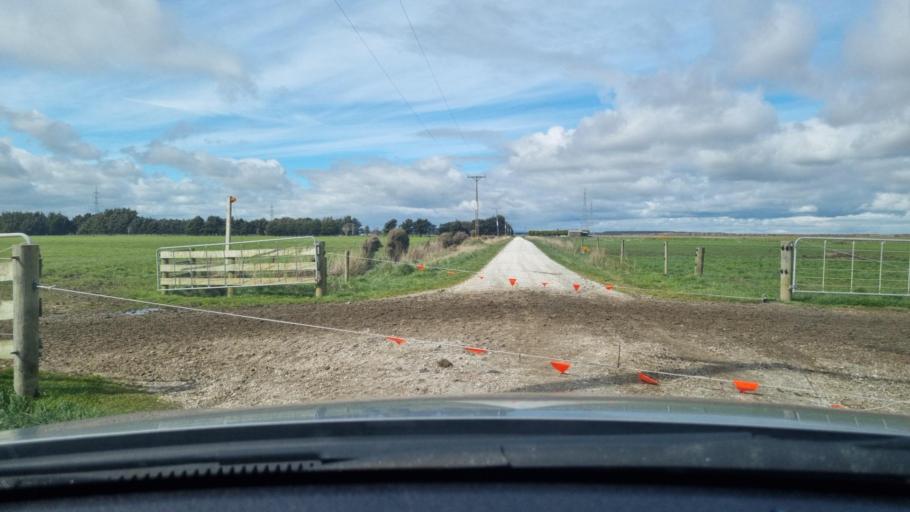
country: NZ
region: Southland
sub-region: Invercargill City
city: Invercargill
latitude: -46.4768
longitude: 168.4268
